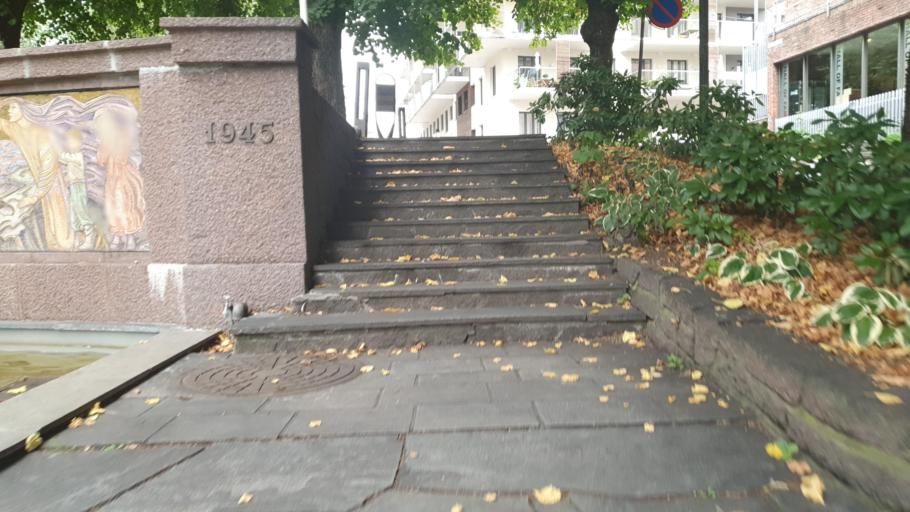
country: NO
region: Vestfold
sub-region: Tonsberg
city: Tonsberg
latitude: 59.2684
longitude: 10.4043
